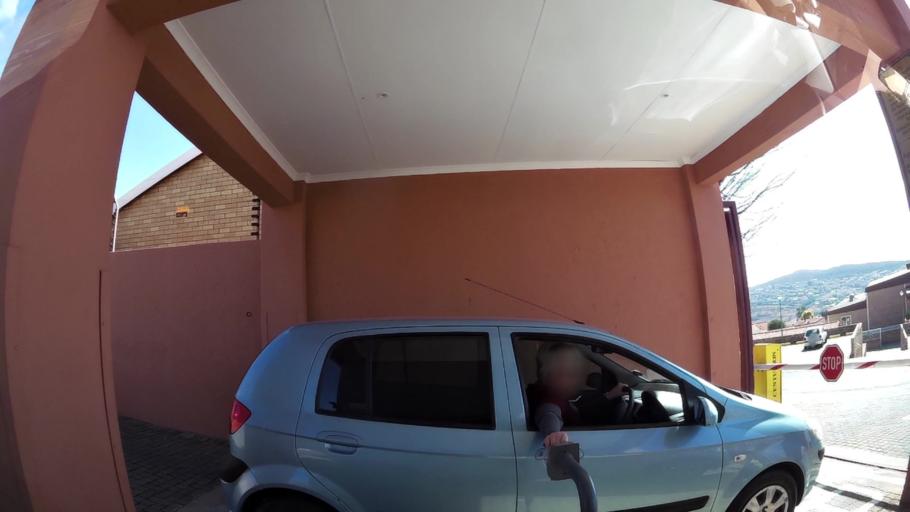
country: ZA
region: Gauteng
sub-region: West Rand District Municipality
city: Krugersdorp
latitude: -26.0978
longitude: 27.8265
